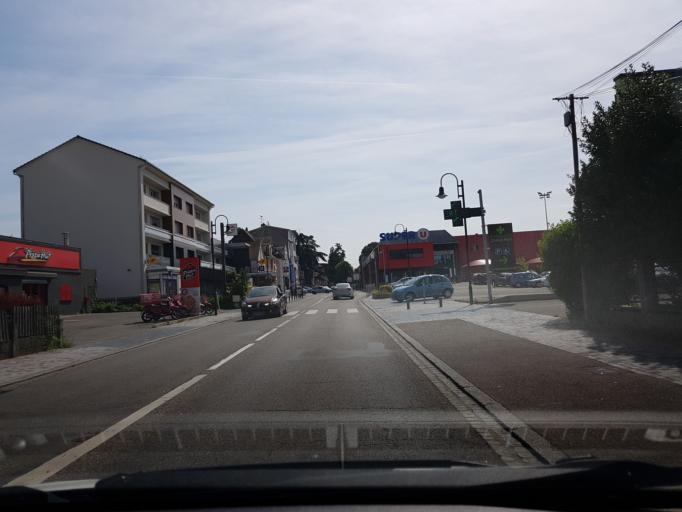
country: FR
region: Alsace
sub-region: Departement du Haut-Rhin
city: Brunstatt
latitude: 47.7268
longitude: 7.3214
